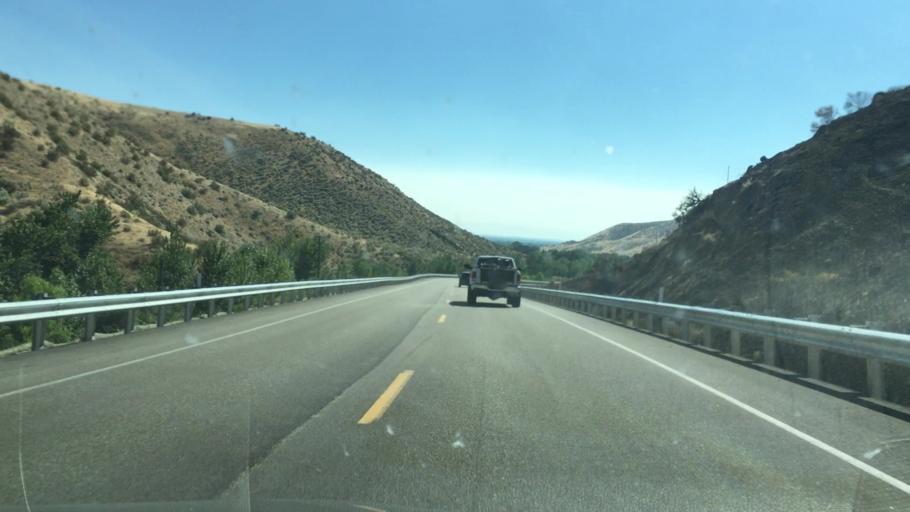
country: US
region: Idaho
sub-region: Ada County
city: Eagle
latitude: 43.7568
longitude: -116.2797
